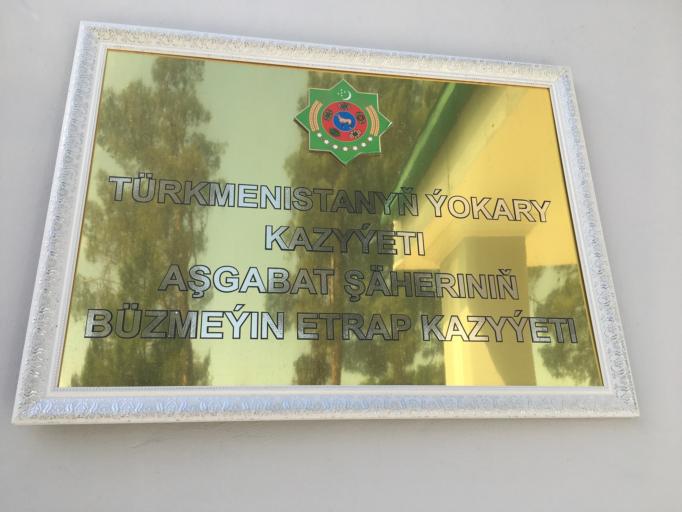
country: TM
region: Ahal
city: Ashgabat
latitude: 37.9364
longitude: 58.2802
